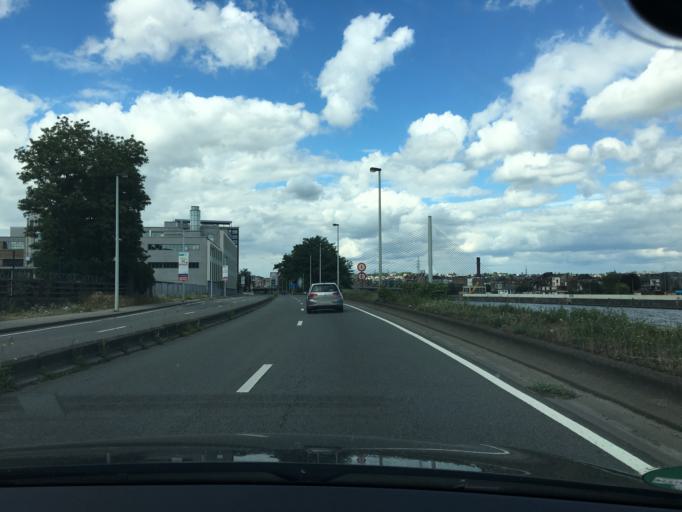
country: BE
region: Wallonia
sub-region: Province de Liege
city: Liege
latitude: 50.6125
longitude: 5.5746
